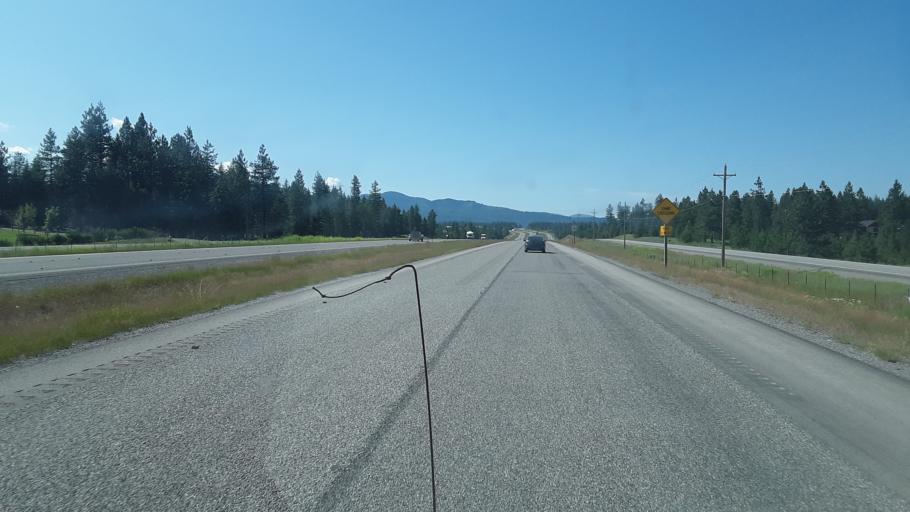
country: US
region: Idaho
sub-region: Kootenai County
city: Spirit Lake
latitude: 47.9744
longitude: -116.6989
